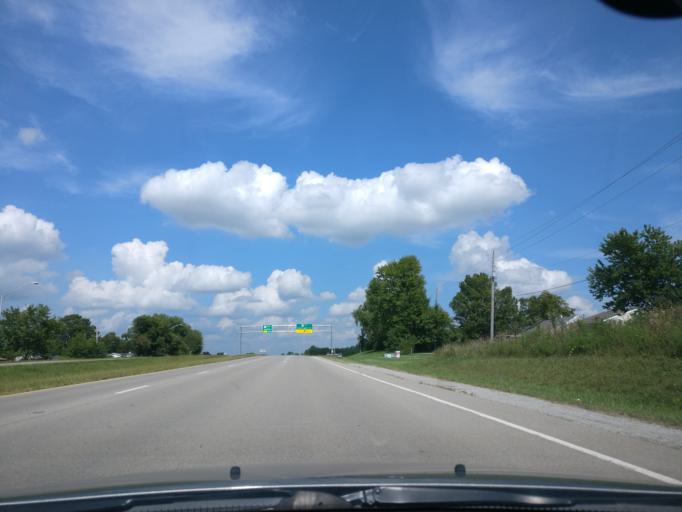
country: US
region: Ohio
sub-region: Greene County
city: Xenia
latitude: 39.6587
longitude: -83.9522
